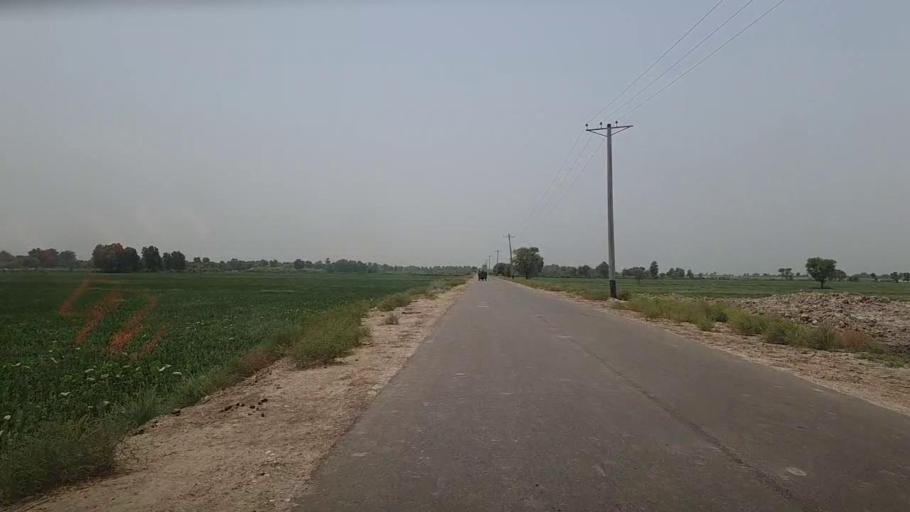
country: PK
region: Sindh
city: Sita Road
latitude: 27.0510
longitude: 67.9020
